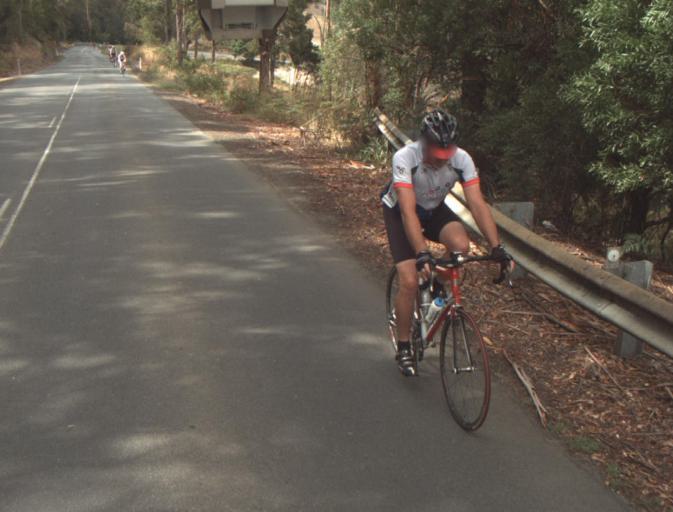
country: AU
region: Tasmania
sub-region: Launceston
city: Mayfield
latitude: -41.2227
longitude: 147.2068
